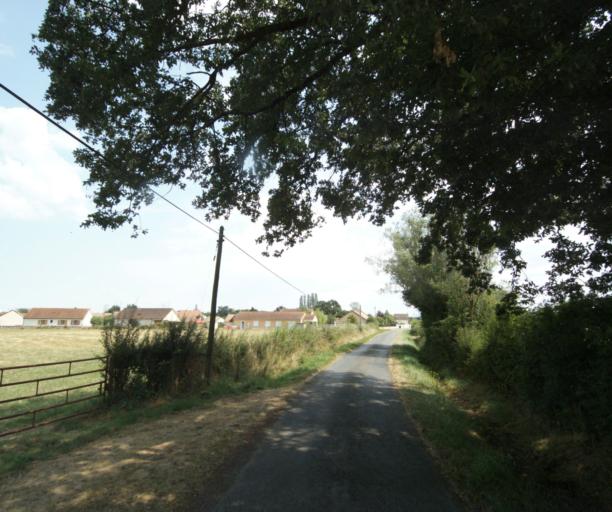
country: FR
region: Bourgogne
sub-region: Departement de Saone-et-Loire
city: Gueugnon
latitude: 46.6011
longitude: 4.0445
